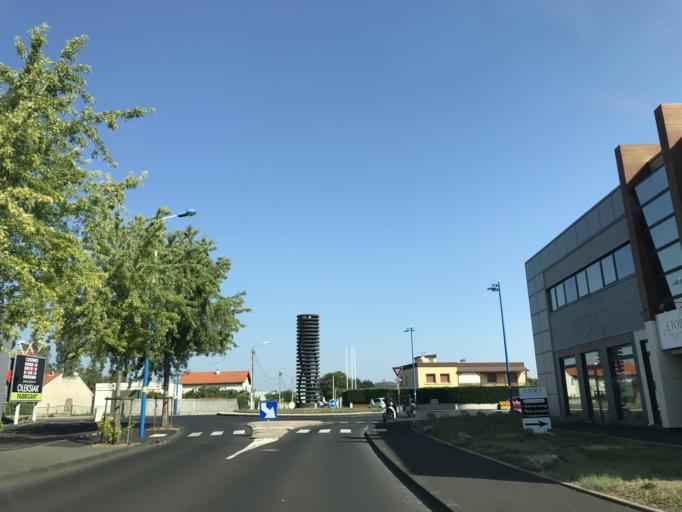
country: FR
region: Auvergne
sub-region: Departement du Puy-de-Dome
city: Perignat-les-Sarlieve
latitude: 45.7532
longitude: 3.1383
